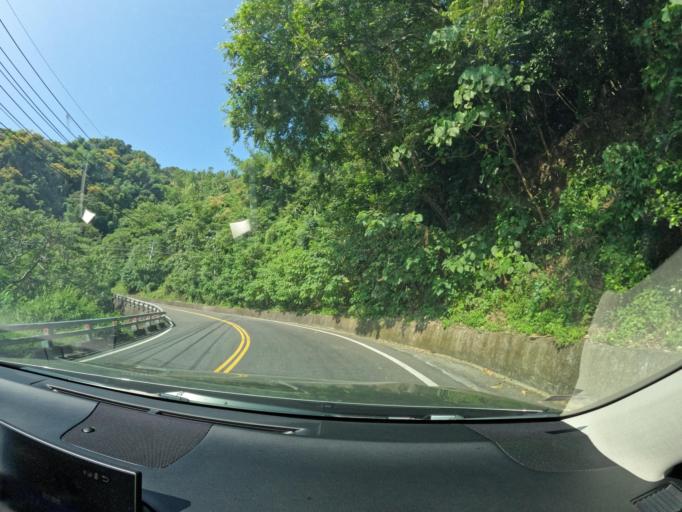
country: TW
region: Taiwan
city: Yujing
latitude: 23.0740
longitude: 120.6220
